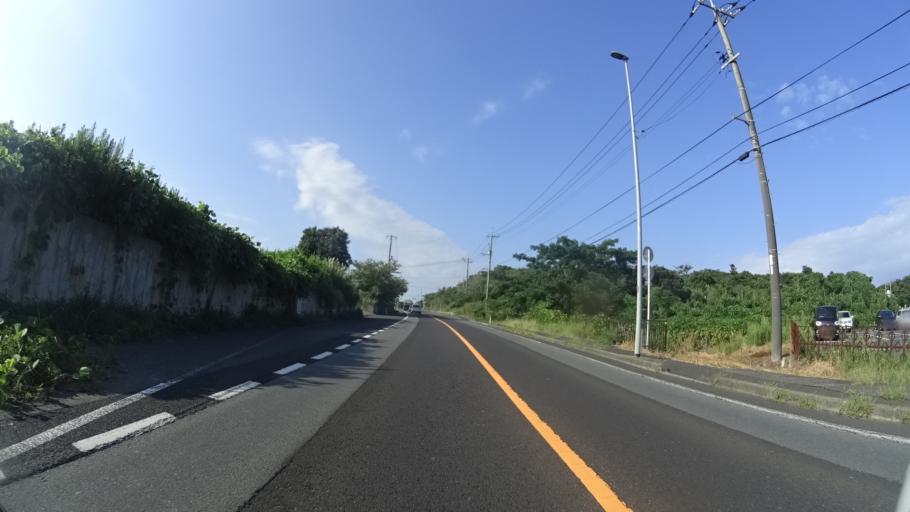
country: JP
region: Shimane
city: Izumo
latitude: 35.3222
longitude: 132.6686
